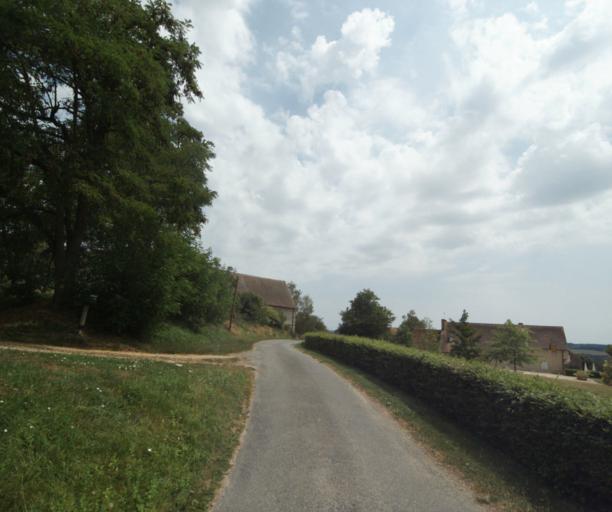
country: FR
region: Bourgogne
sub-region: Departement de Saone-et-Loire
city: Gueugnon
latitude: 46.5801
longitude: 4.0368
